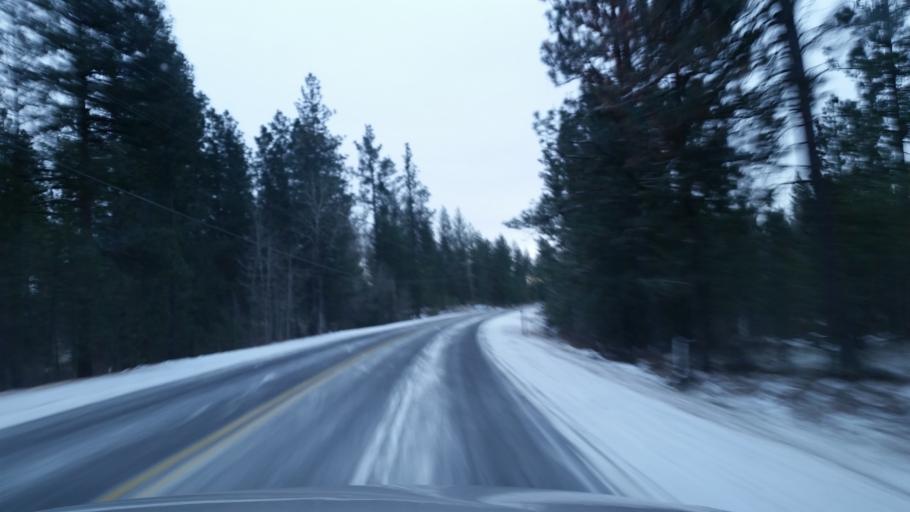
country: US
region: Washington
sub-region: Spokane County
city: Cheney
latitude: 47.4673
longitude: -117.5376
